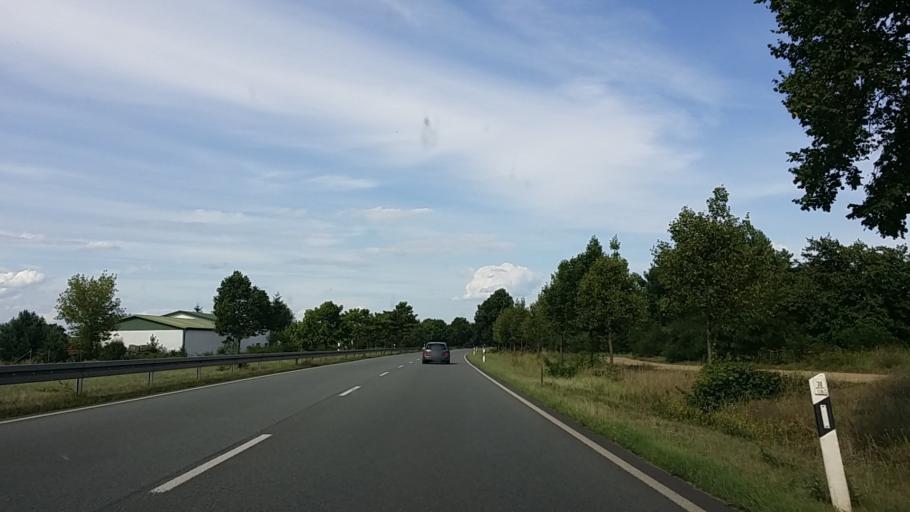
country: DE
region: Brandenburg
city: Wittenberge
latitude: 53.0100
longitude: 11.7235
